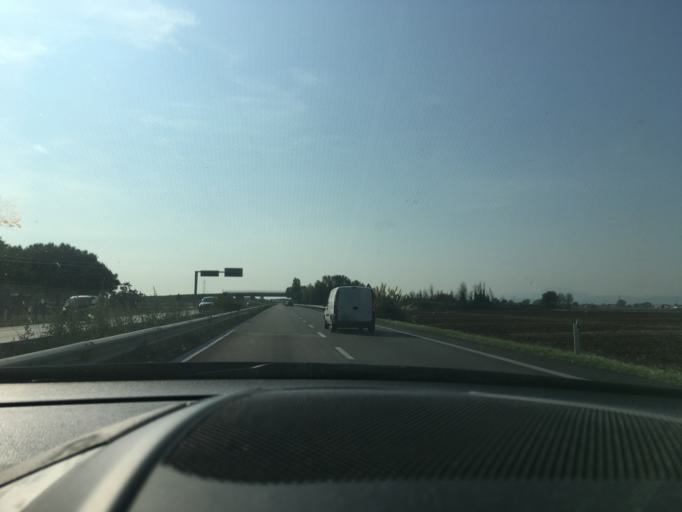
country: IT
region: Emilia-Romagna
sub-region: Provincia di Rimini
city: Bellaria-Igea Marina
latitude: 44.1226
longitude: 12.4721
